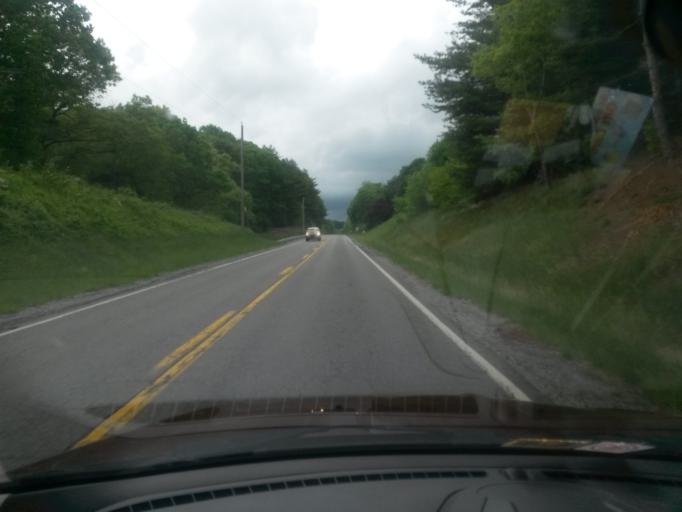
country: US
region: Virginia
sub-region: Floyd County
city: Floyd
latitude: 36.9416
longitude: -80.3513
